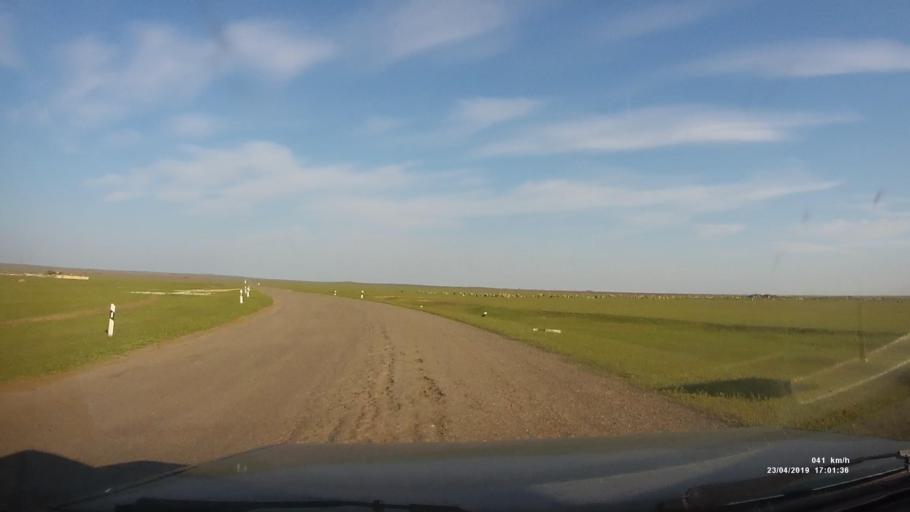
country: RU
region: Kalmykiya
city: Priyutnoye
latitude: 46.2949
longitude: 43.4085
